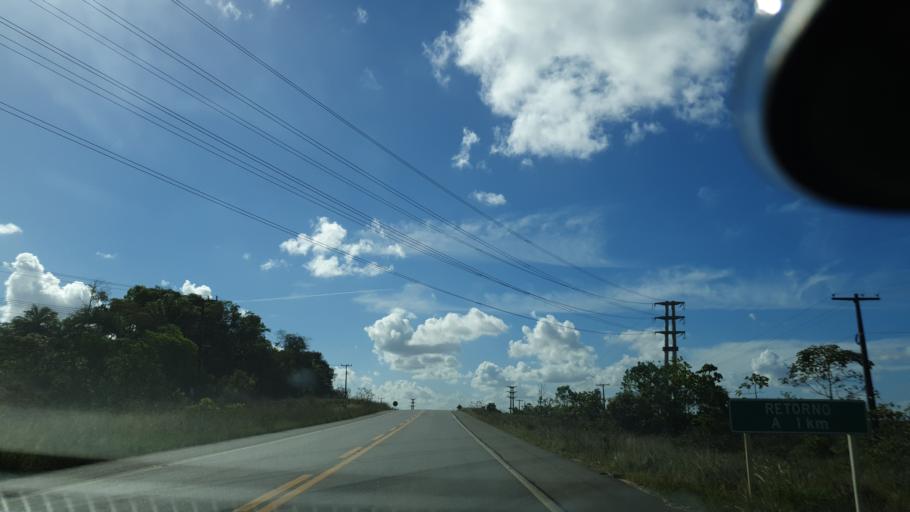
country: BR
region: Bahia
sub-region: Camacari
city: Camacari
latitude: -12.6822
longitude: -38.2388
